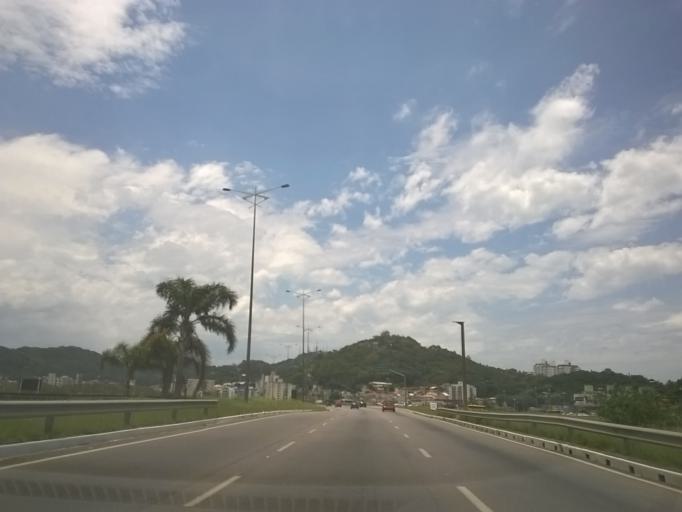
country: BR
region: Santa Catarina
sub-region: Florianopolis
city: Saco dos Limoes
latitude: -27.6179
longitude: -48.5282
